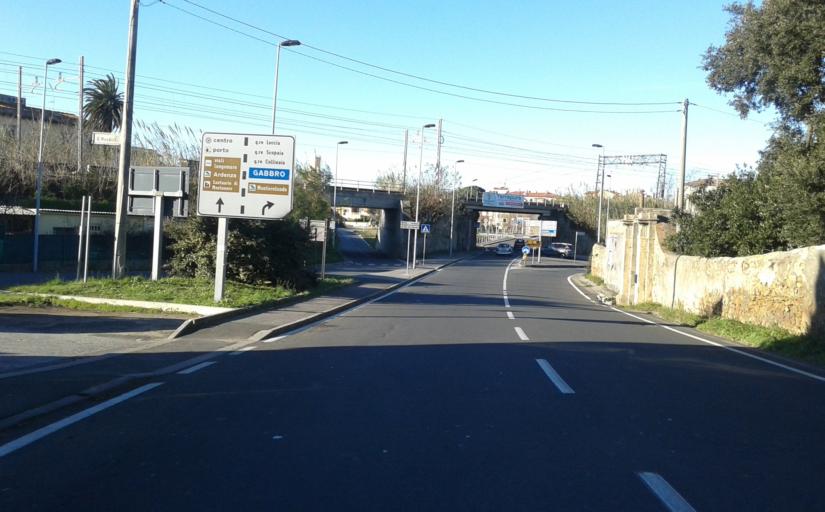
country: IT
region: Tuscany
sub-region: Provincia di Livorno
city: Livorno
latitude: 43.5129
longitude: 10.3269
